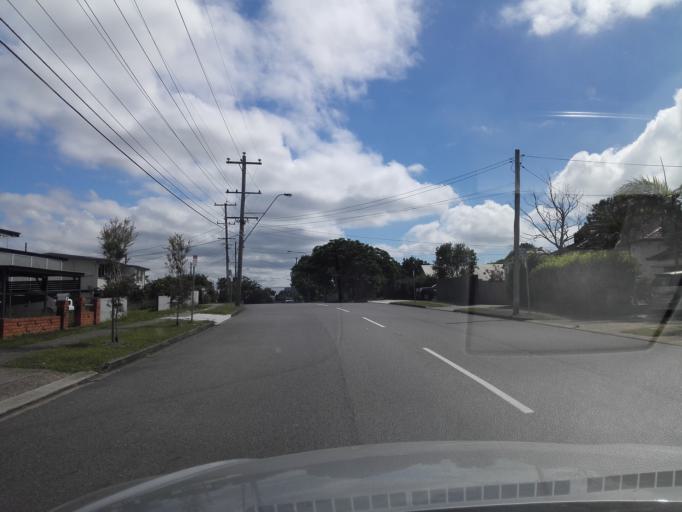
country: AU
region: Queensland
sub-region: Brisbane
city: Zillmere
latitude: -27.3604
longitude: 153.0332
